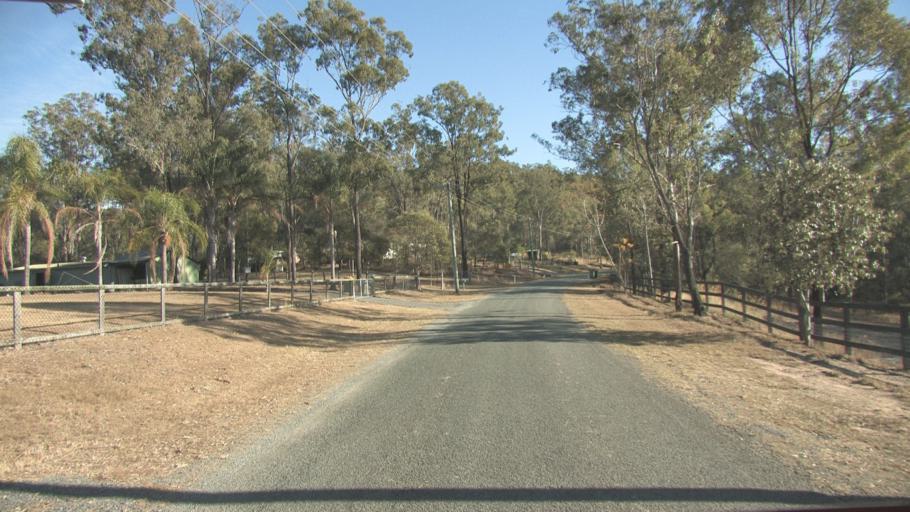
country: AU
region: Queensland
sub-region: Logan
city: Cedar Vale
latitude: -27.8540
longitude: 153.0831
